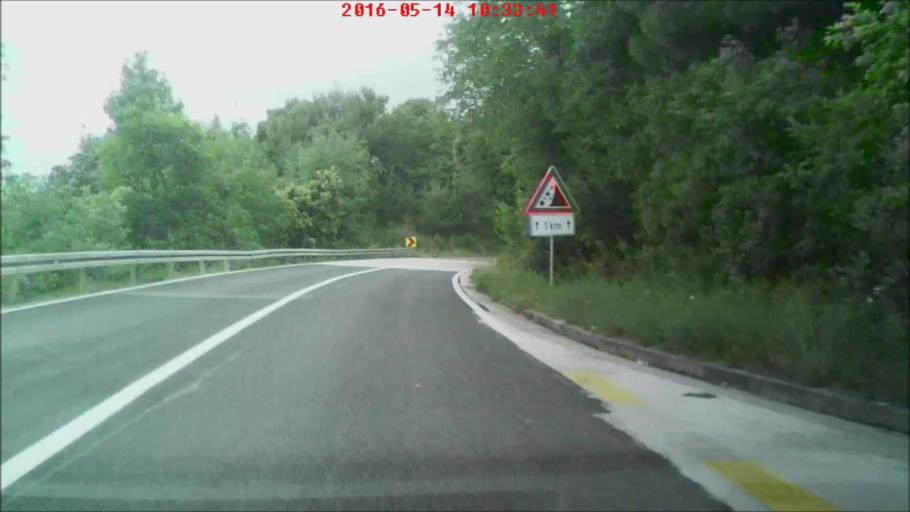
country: HR
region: Dubrovacko-Neretvanska
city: Podgora
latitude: 42.7757
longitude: 17.8879
